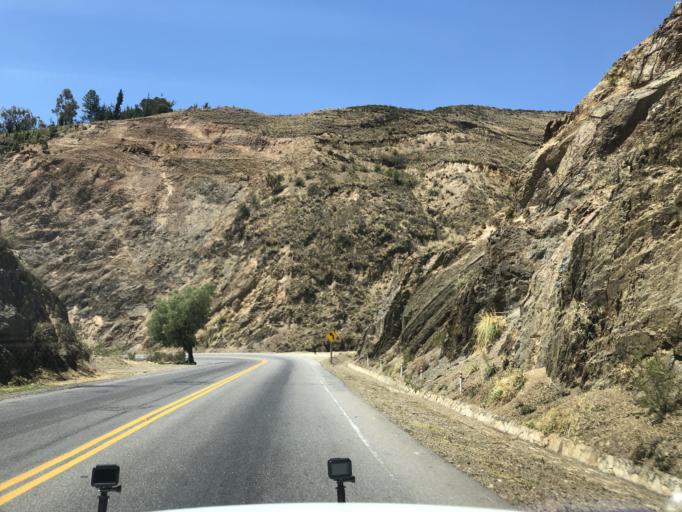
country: BO
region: Cochabamba
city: Irpa Irpa
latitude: -17.6688
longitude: -66.4258
